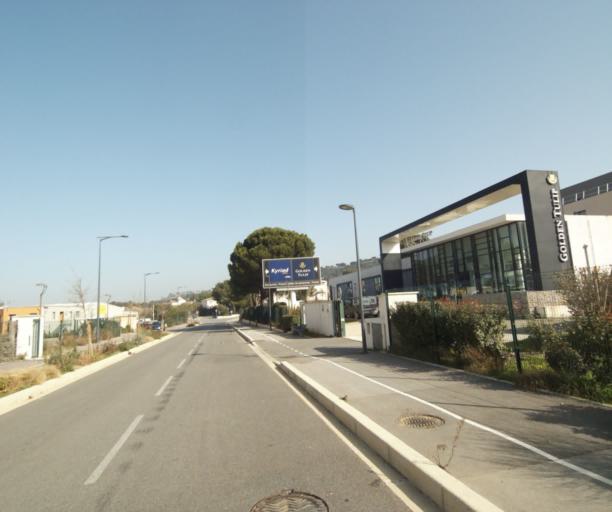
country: FR
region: Provence-Alpes-Cote d'Azur
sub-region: Departement des Bouches-du-Rhone
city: Vitrolles
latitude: 43.4459
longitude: 5.2338
